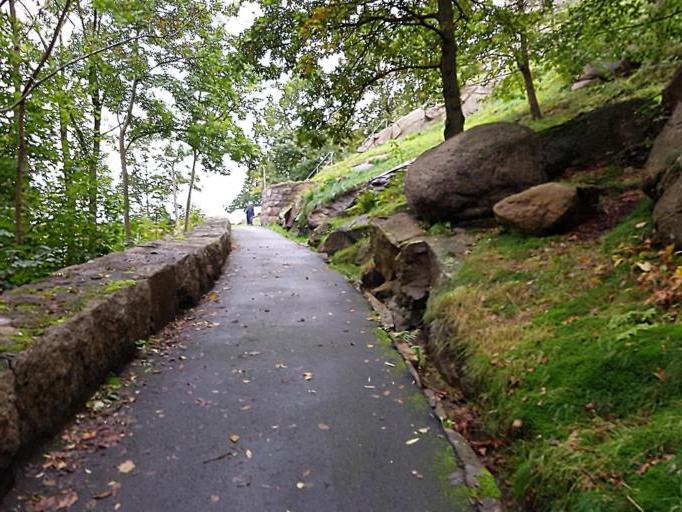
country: SE
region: Vaestra Goetaland
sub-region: Goteborg
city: Goeteborg
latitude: 57.7140
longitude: 11.9391
